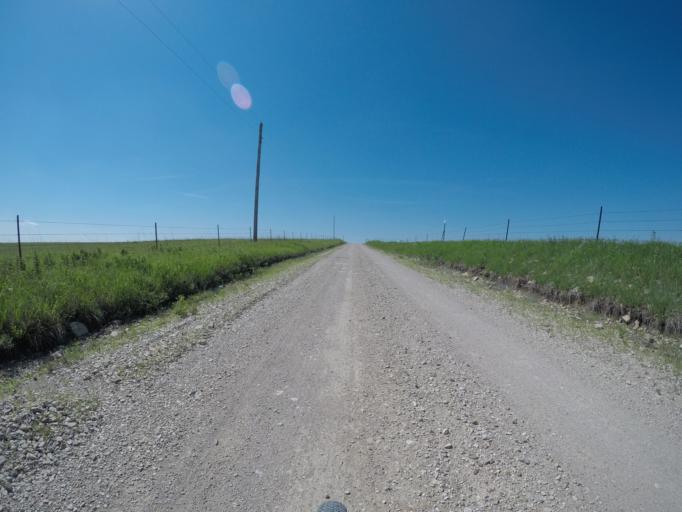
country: US
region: Kansas
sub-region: Wabaunsee County
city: Alma
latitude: 39.0111
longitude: -96.1783
